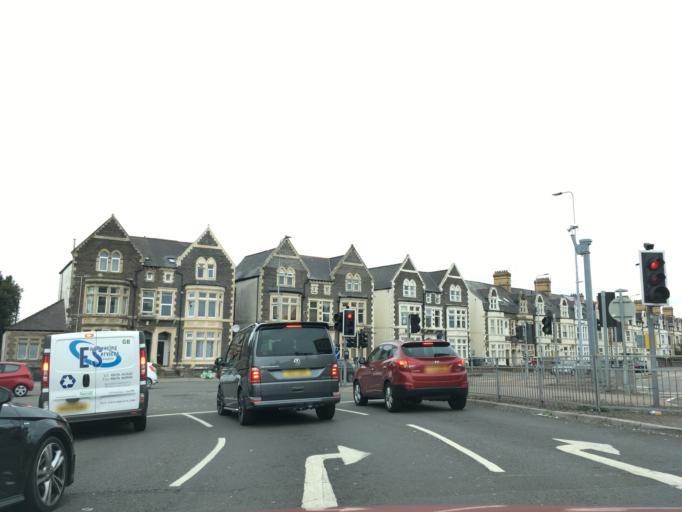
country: GB
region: Wales
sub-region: Cardiff
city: Cardiff
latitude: 51.4909
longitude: -3.1509
